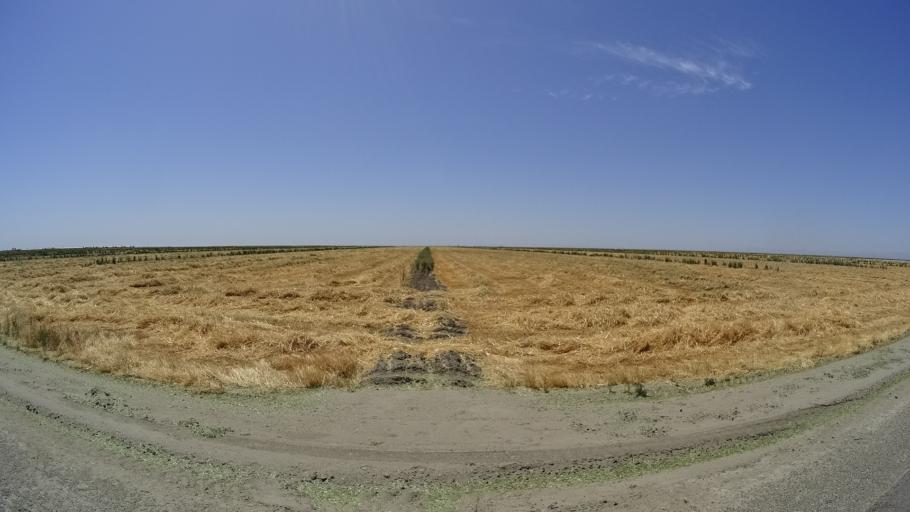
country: US
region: California
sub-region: Kings County
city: Corcoran
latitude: 36.1379
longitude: -119.6770
